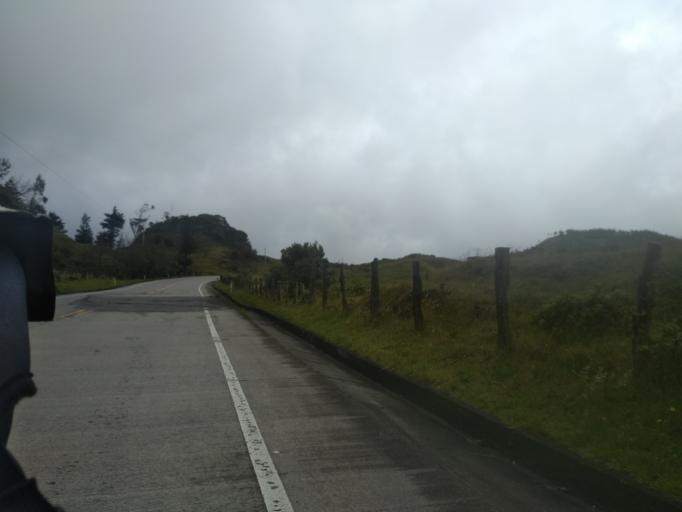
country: EC
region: Loja
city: Loja
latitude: -3.8833
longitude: -79.2641
